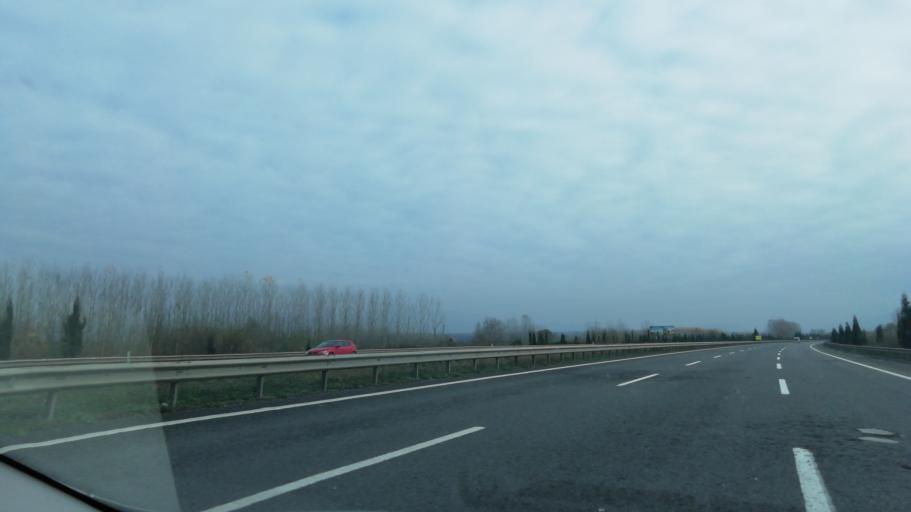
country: TR
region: Sakarya
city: Akyazi
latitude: 40.7409
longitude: 30.6544
